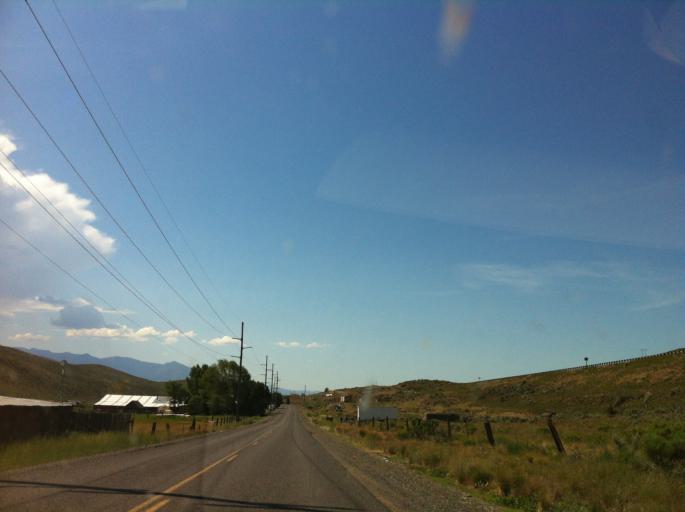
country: US
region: Oregon
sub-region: Baker County
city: Baker City
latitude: 44.7159
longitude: -117.7740
